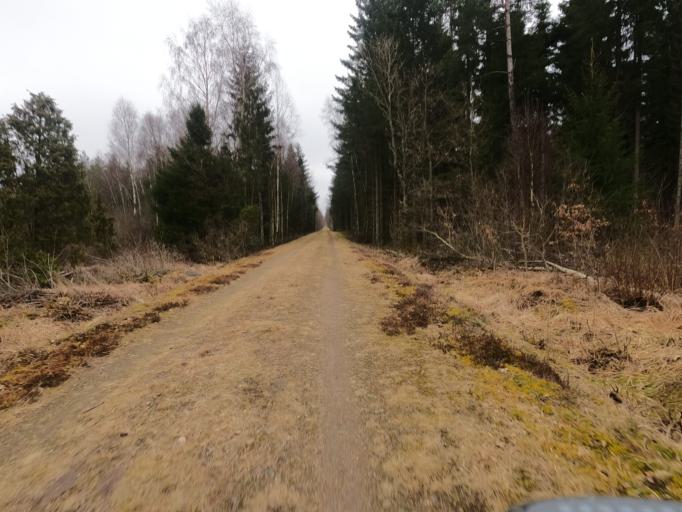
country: SE
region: Kronoberg
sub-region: Ljungby Kommun
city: Ljungby
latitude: 56.8242
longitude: 13.7370
